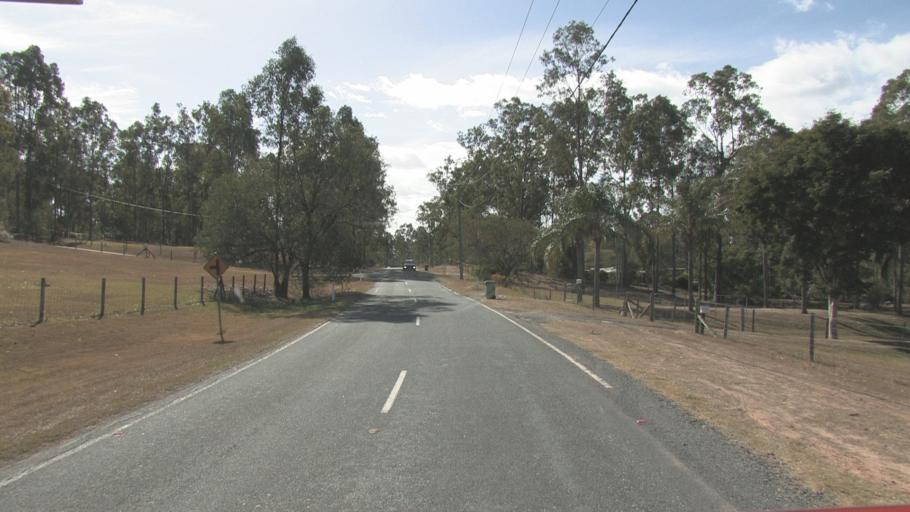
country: AU
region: Queensland
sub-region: Logan
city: Cedar Vale
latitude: -27.8831
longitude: 152.9963
